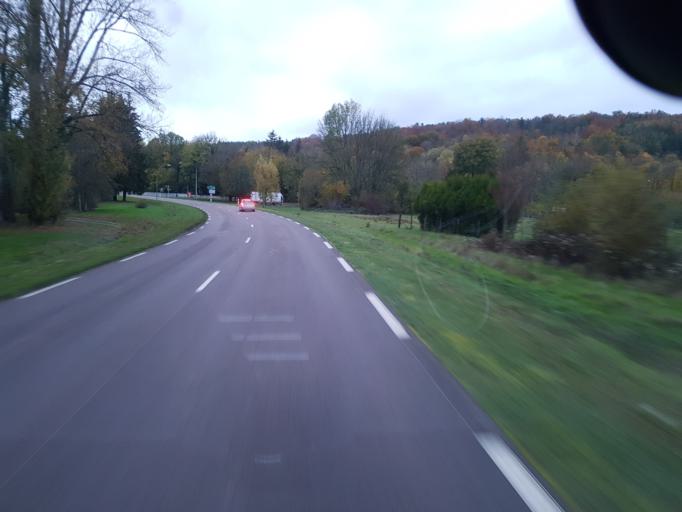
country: FR
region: Champagne-Ardenne
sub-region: Departement de l'Aube
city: Mussy-sur-Seine
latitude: 47.9795
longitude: 4.5003
